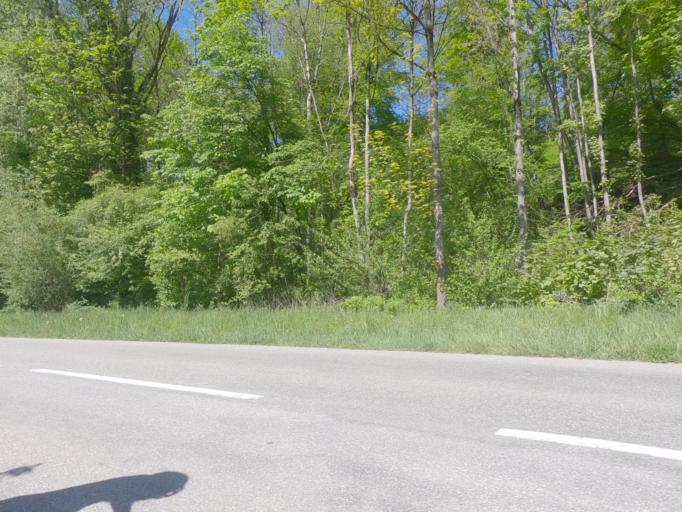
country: CH
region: Solothurn
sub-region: Bezirk Wasseramt
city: Luterbach
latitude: 47.2289
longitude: 7.5867
